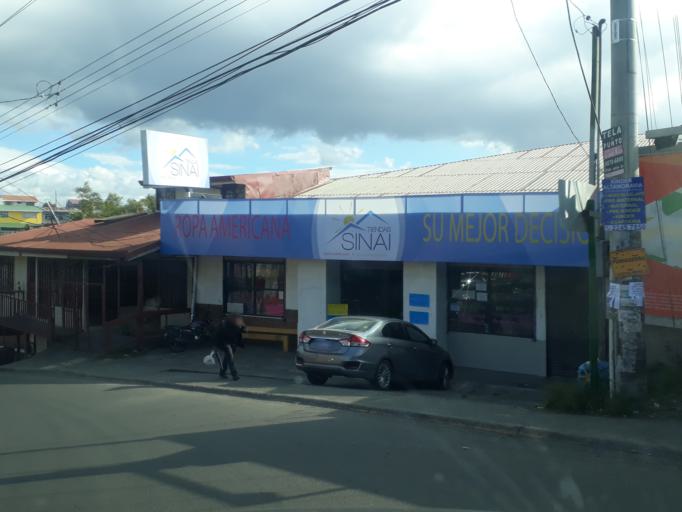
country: CR
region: San Jose
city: Purral
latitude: 9.9680
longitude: -84.0349
